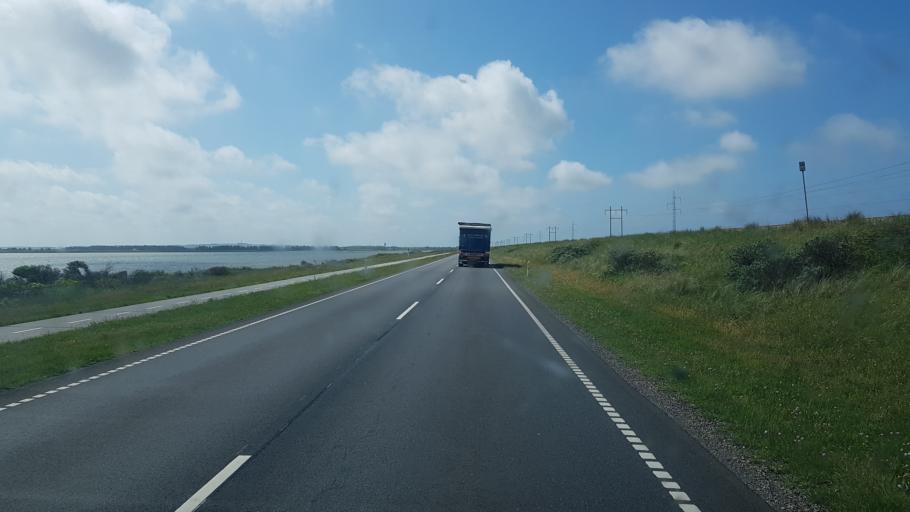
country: DK
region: Central Jutland
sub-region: Lemvig Kommune
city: Harboore
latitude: 56.6449
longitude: 8.1900
